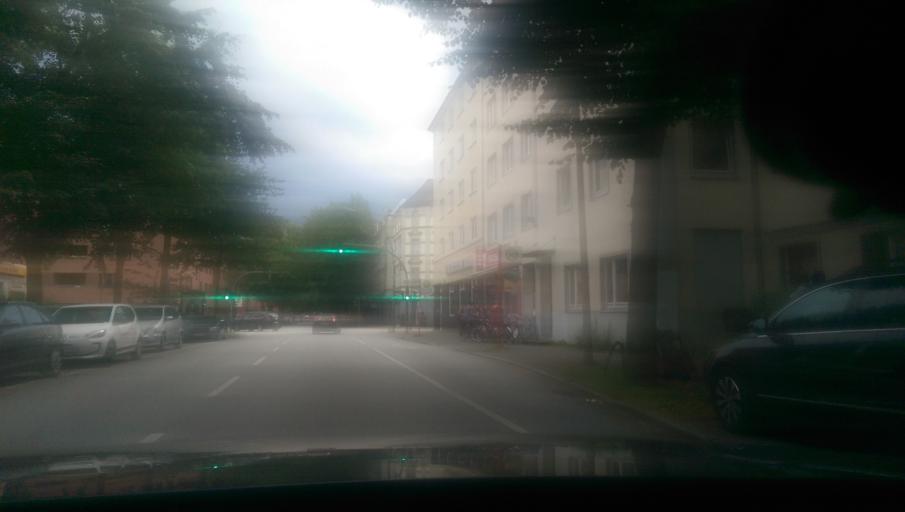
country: DE
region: Hamburg
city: Kleiner Grasbrook
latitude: 53.5111
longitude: 9.9867
